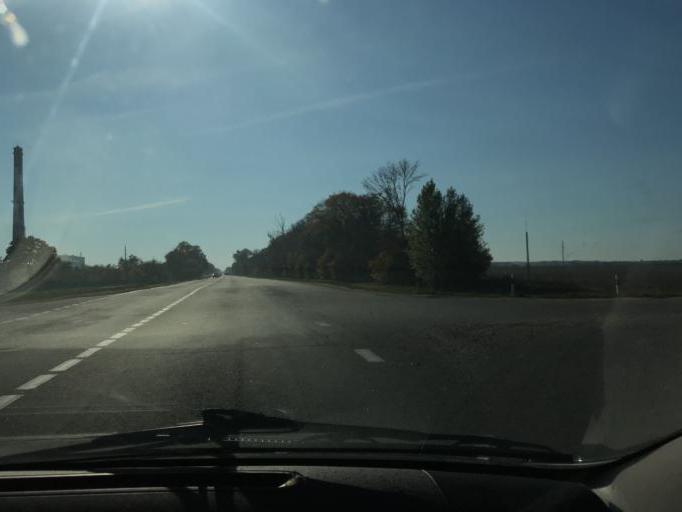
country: BY
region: Minsk
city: Starobin
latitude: 52.8005
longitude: 27.4646
